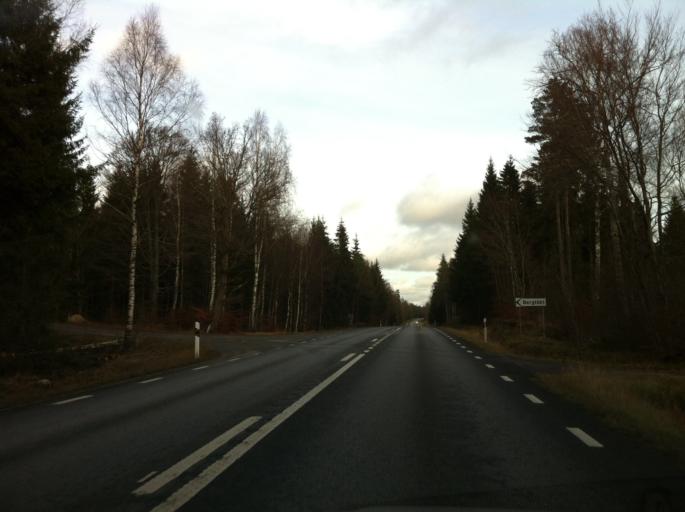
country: SE
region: Kronoberg
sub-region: Alvesta Kommun
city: Vislanda
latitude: 56.7621
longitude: 14.5246
